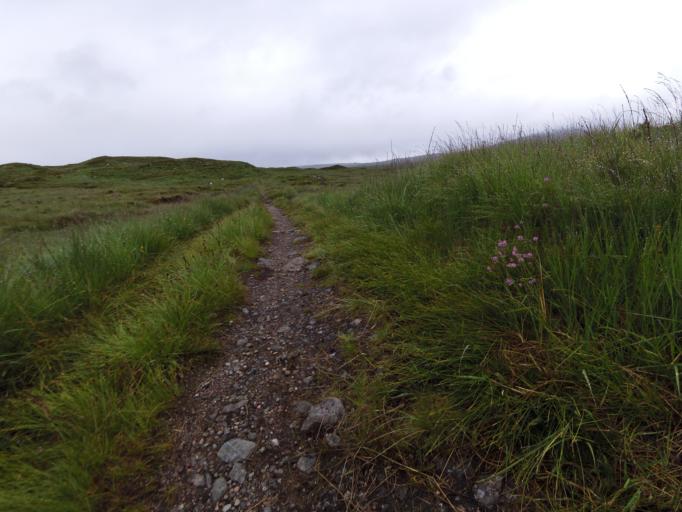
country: GB
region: Scotland
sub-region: Highland
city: Spean Bridge
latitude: 56.7676
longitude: -4.7035
